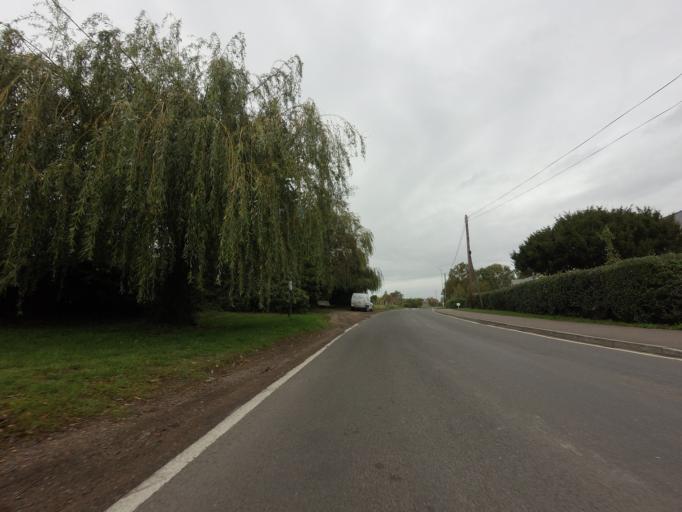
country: GB
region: England
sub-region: Cambridgeshire
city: Harston
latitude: 52.0956
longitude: 0.0701
